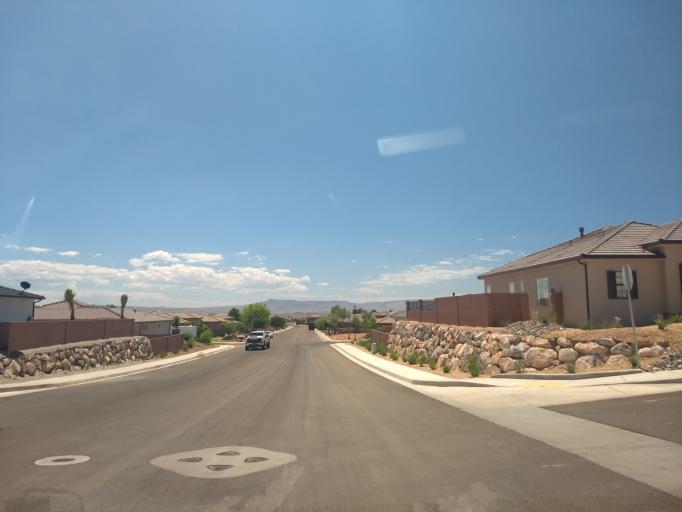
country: US
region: Utah
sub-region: Washington County
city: Washington
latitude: 37.1573
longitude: -113.5217
